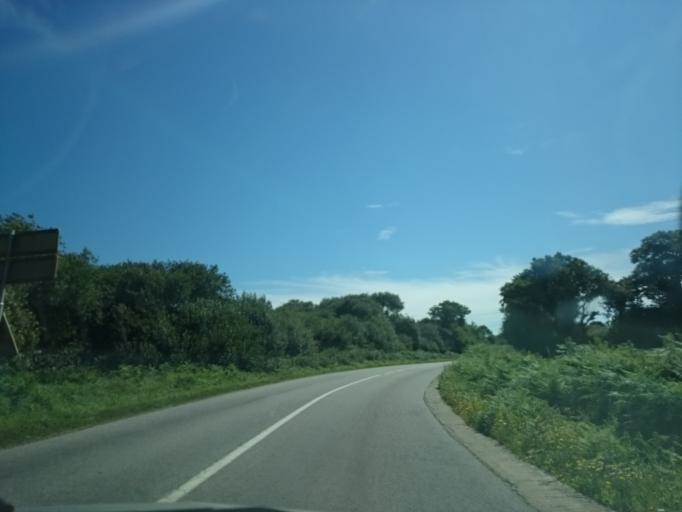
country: FR
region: Brittany
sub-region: Departement du Finistere
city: Saint-Renan
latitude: 48.4401
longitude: -4.6437
